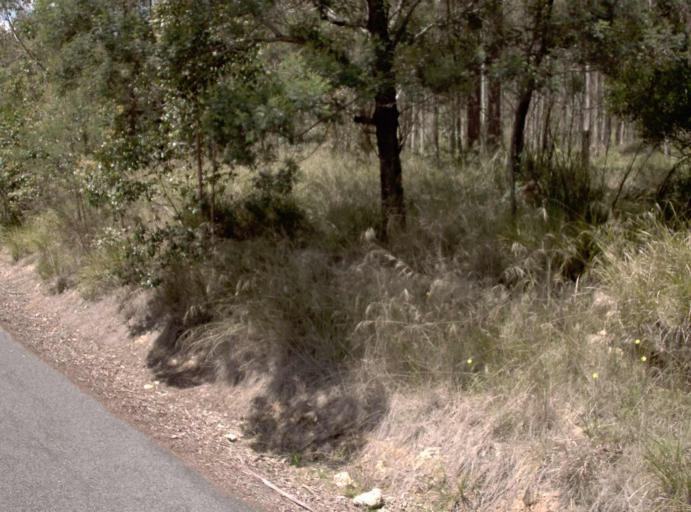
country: AU
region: New South Wales
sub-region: Bombala
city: Bombala
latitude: -37.4003
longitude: 149.0128
